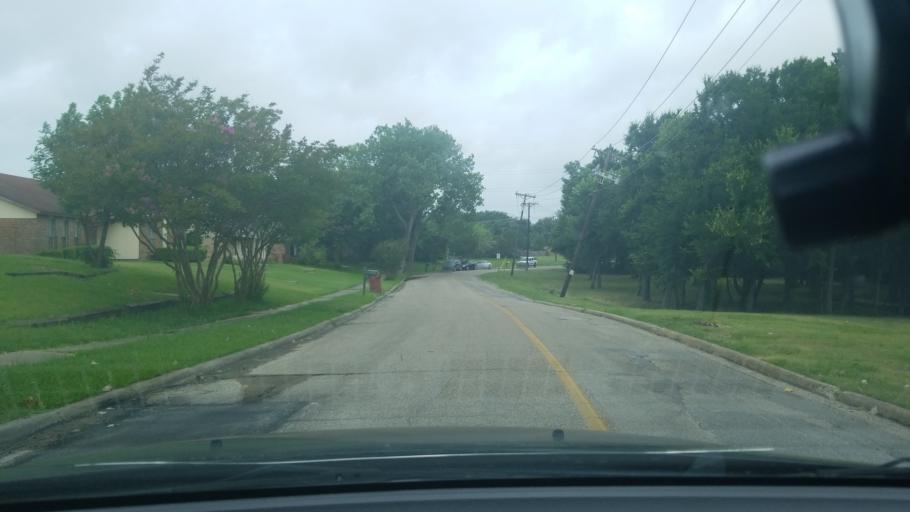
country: US
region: Texas
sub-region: Dallas County
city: Mesquite
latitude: 32.7875
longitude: -96.6420
